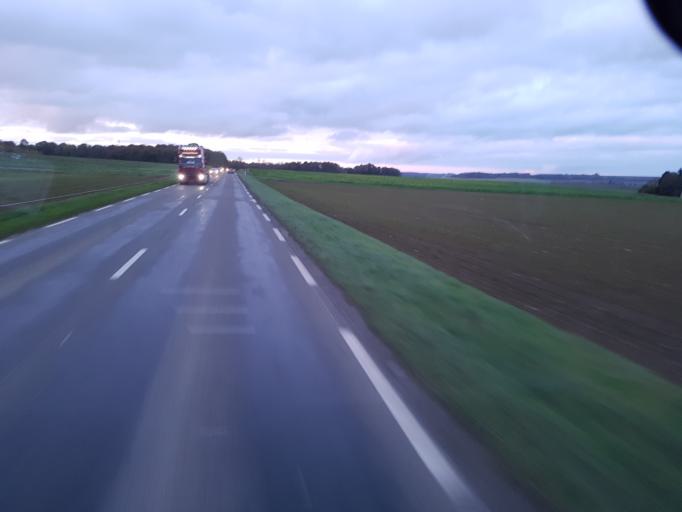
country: FR
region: Picardie
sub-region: Departement de l'Aisne
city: Coincy
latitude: 49.1662
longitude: 3.3778
